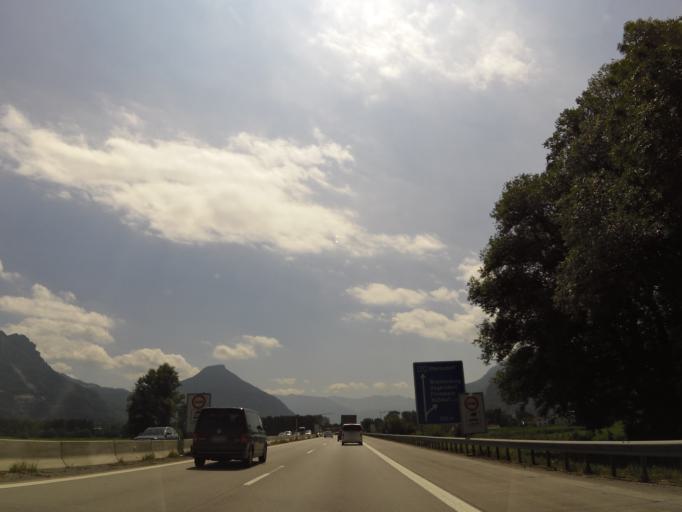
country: DE
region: Bavaria
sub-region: Upper Bavaria
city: Flintsbach
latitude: 47.7432
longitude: 12.1238
